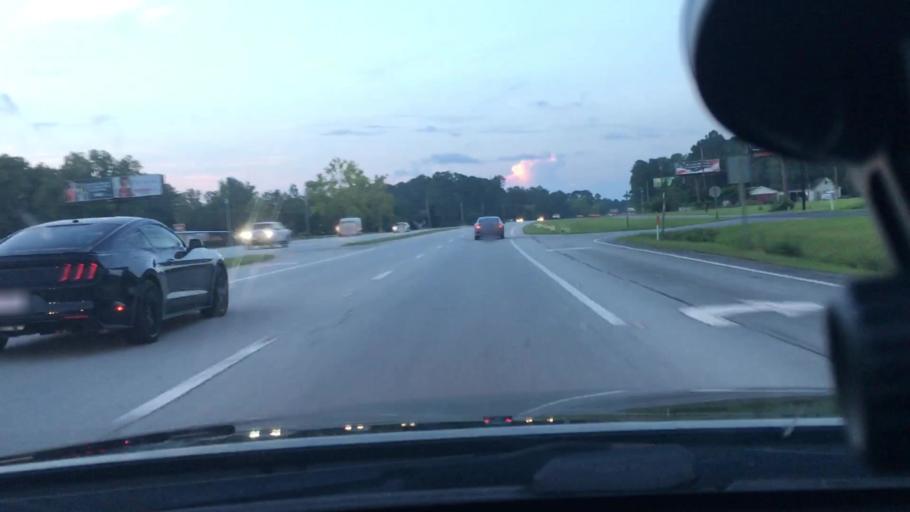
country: US
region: North Carolina
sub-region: Craven County
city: Neuse Forest
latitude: 34.9541
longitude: -76.9494
